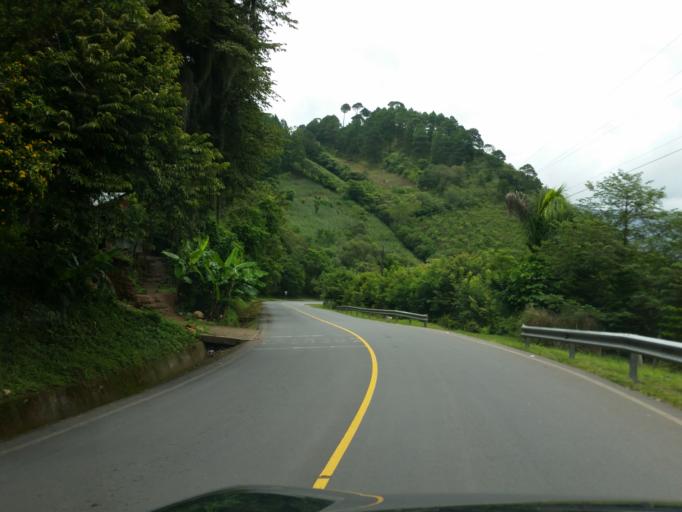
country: NI
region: Matagalpa
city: Matagalpa
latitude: 12.9720
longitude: -85.9205
